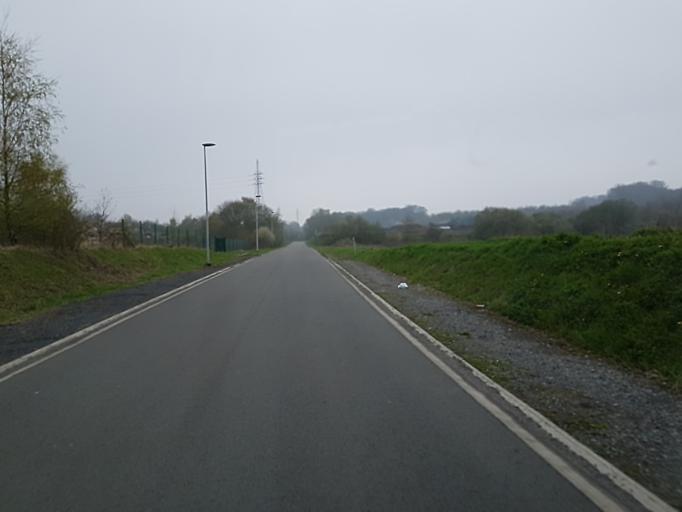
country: BE
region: Wallonia
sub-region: Province du Hainaut
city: Jurbise
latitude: 50.4863
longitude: 3.8964
